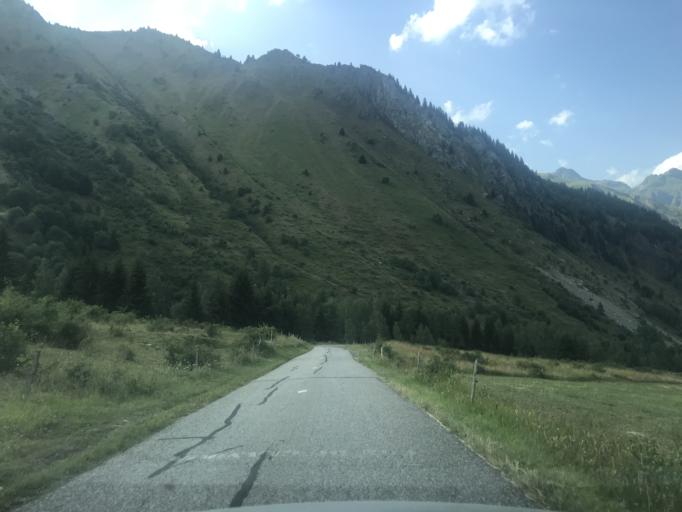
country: FR
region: Rhone-Alpes
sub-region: Departement de la Savoie
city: Saint-Etienne-de-Cuines
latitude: 45.2600
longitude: 6.1951
